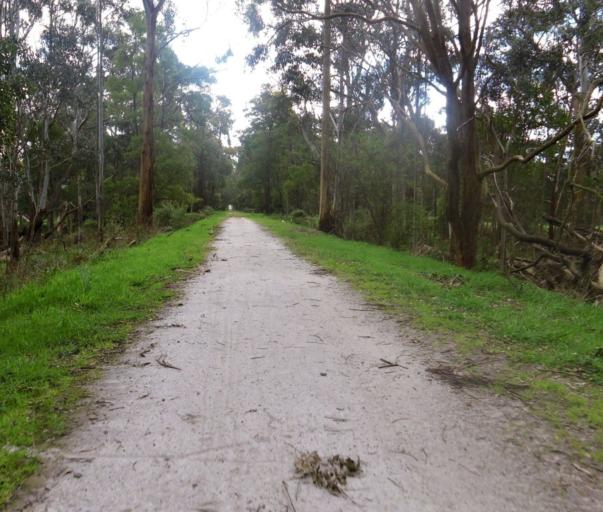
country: AU
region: Victoria
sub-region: Bass Coast
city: North Wonthaggi
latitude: -38.5984
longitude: 146.0467
